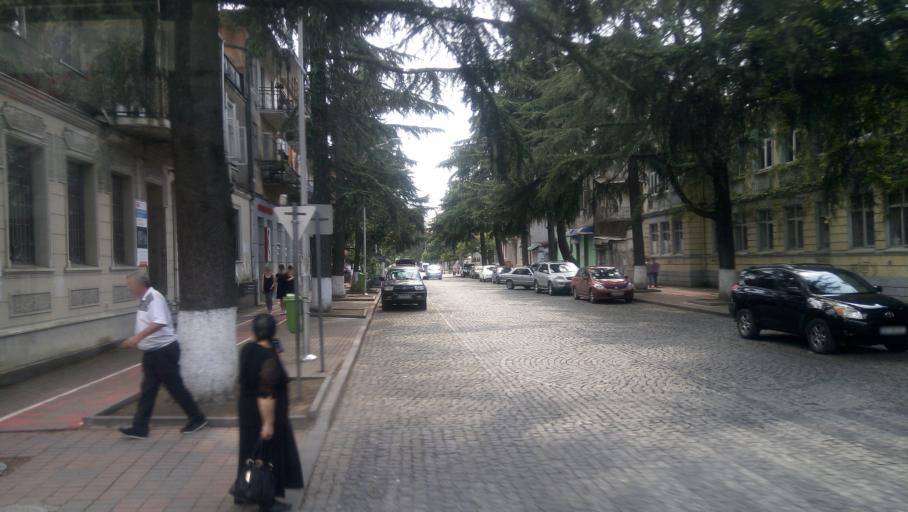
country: GE
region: Ajaria
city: Batumi
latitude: 41.6485
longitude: 41.6378
